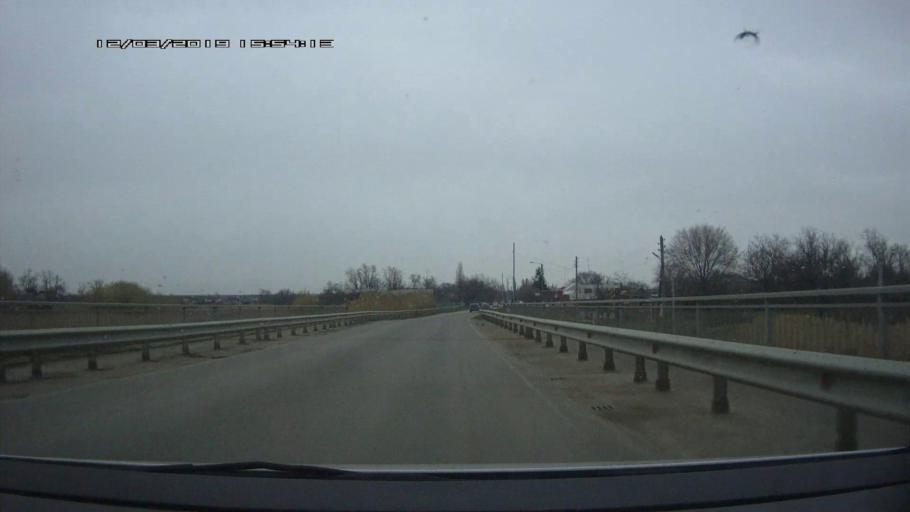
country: RU
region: Rostov
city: Novobataysk
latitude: 46.8894
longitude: 39.7772
